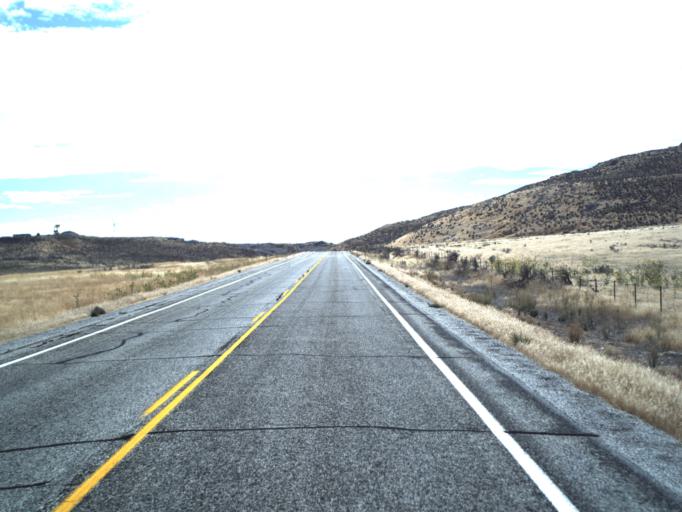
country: US
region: Utah
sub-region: Box Elder County
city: Tremonton
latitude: 41.6880
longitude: -112.4441
